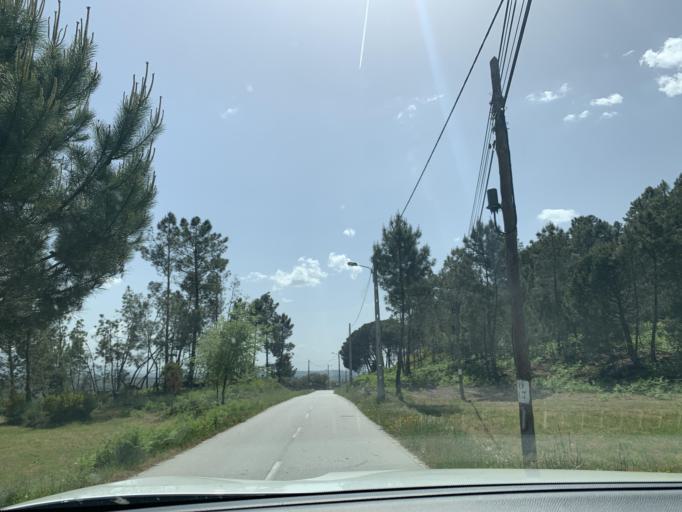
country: PT
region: Guarda
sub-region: Fornos de Algodres
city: Fornos de Algodres
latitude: 40.5822
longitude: -7.6356
